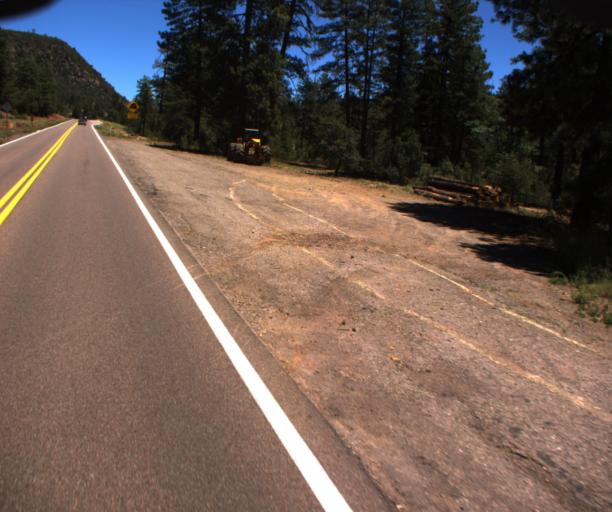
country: US
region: Arizona
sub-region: Gila County
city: Pine
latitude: 34.4064
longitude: -111.4884
